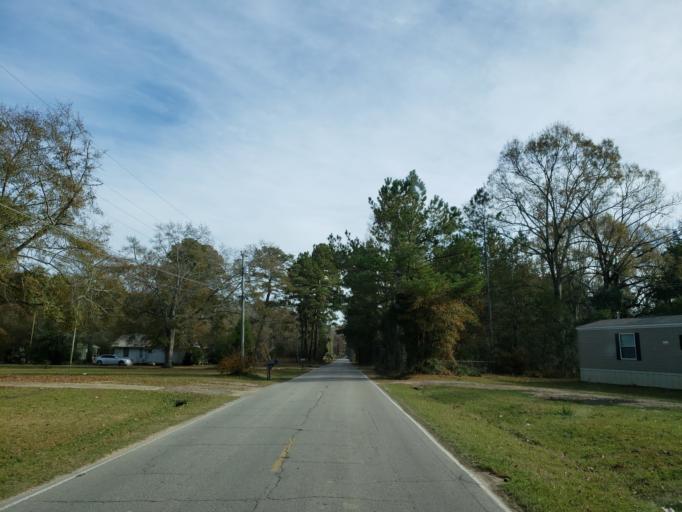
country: US
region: Mississippi
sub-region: Forrest County
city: Rawls Springs
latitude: 31.3982
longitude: -89.3910
